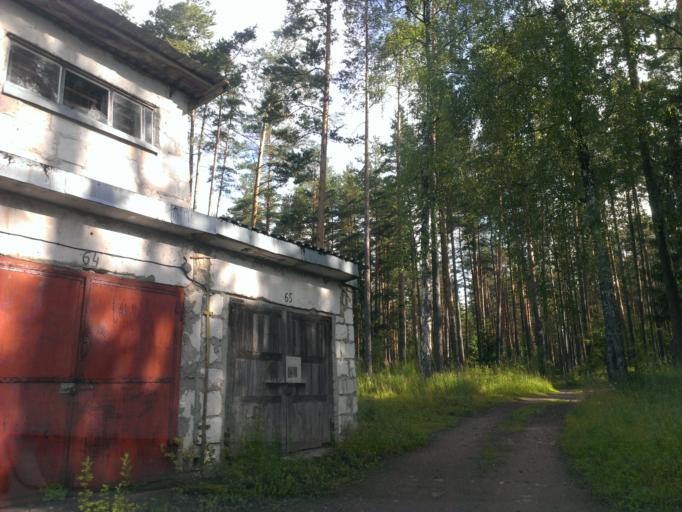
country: LV
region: Incukalns
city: Vangazi
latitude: 57.0996
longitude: 24.5378
